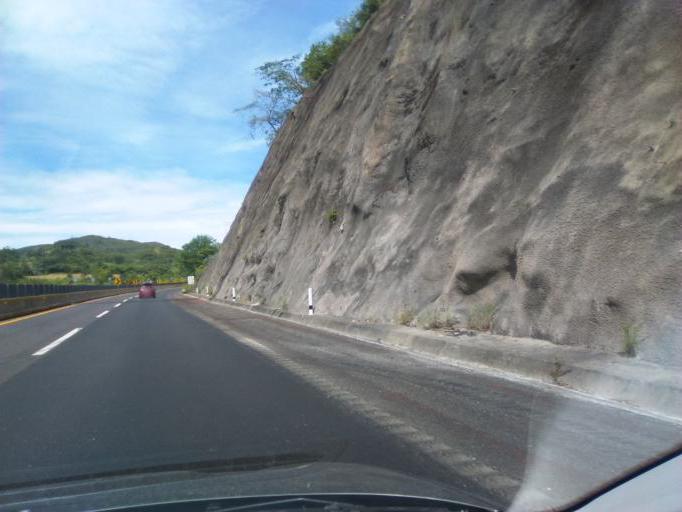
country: MX
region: Guerrero
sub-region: Chilpancingo de los Bravo
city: Acahuizotla
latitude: 17.3785
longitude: -99.4758
